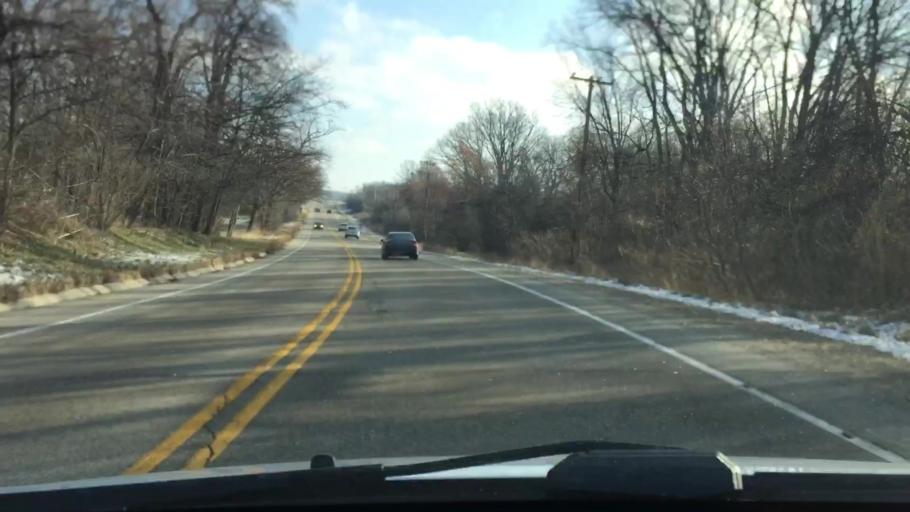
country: US
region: Wisconsin
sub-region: Waukesha County
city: Dousman
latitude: 43.0182
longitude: -88.4322
